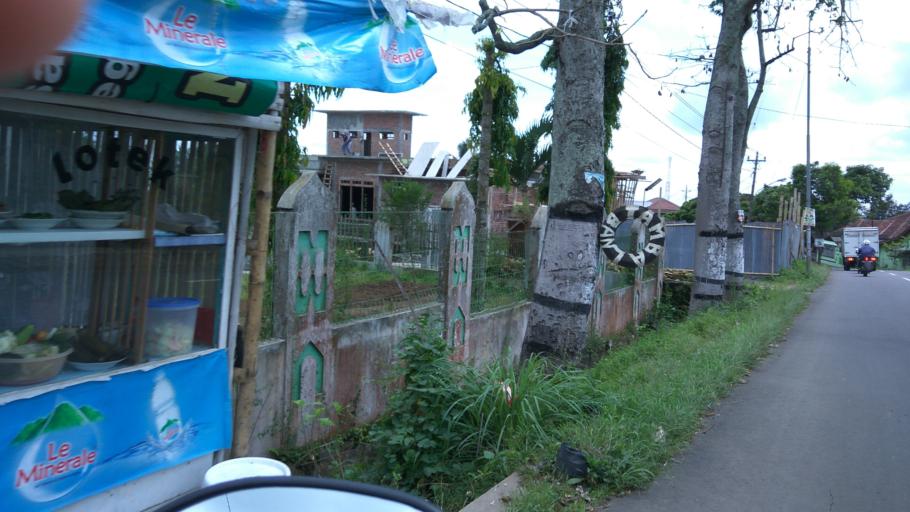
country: ID
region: Central Java
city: Ambarawa
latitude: -7.2351
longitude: 110.3804
